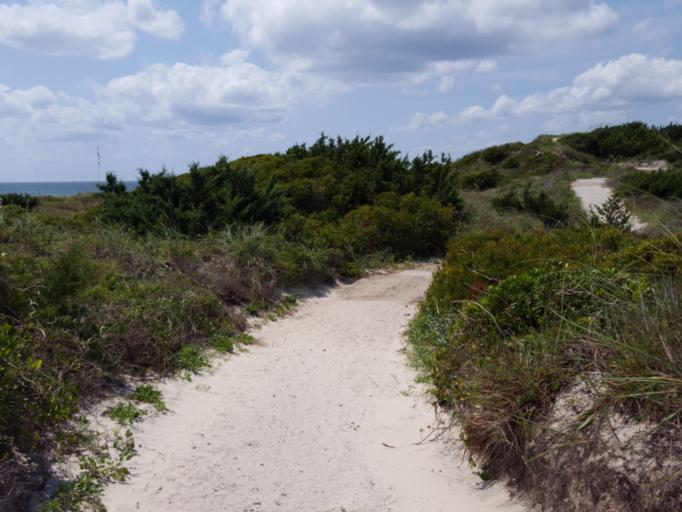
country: US
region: North Carolina
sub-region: Carteret County
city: Beaufort
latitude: 34.6947
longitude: -76.6809
